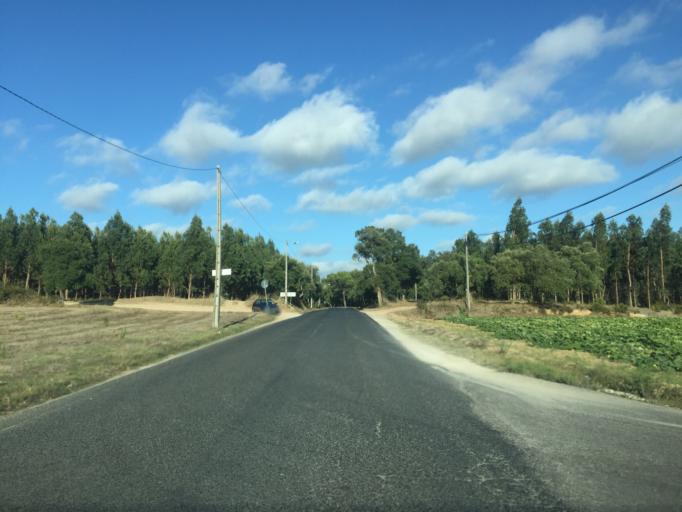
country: PT
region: Lisbon
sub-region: Torres Vedras
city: A dos Cunhados
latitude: 39.1458
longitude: -9.2809
